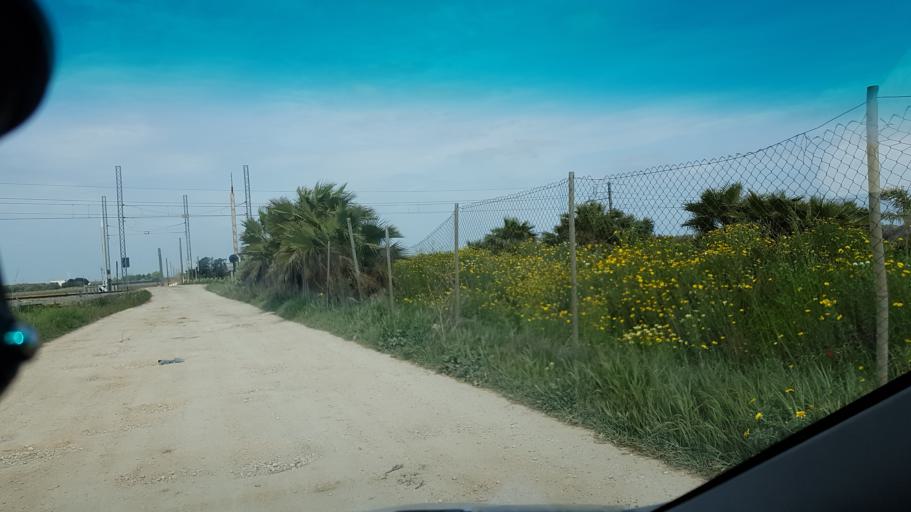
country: IT
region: Apulia
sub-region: Provincia di Brindisi
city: Mesagne
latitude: 40.5944
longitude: 17.8580
